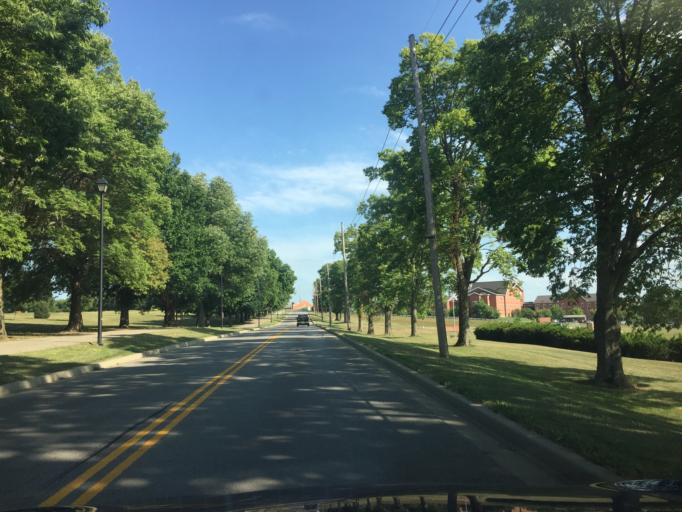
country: US
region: Kansas
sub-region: Leavenworth County
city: Leavenworth
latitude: 39.3463
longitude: -94.9289
